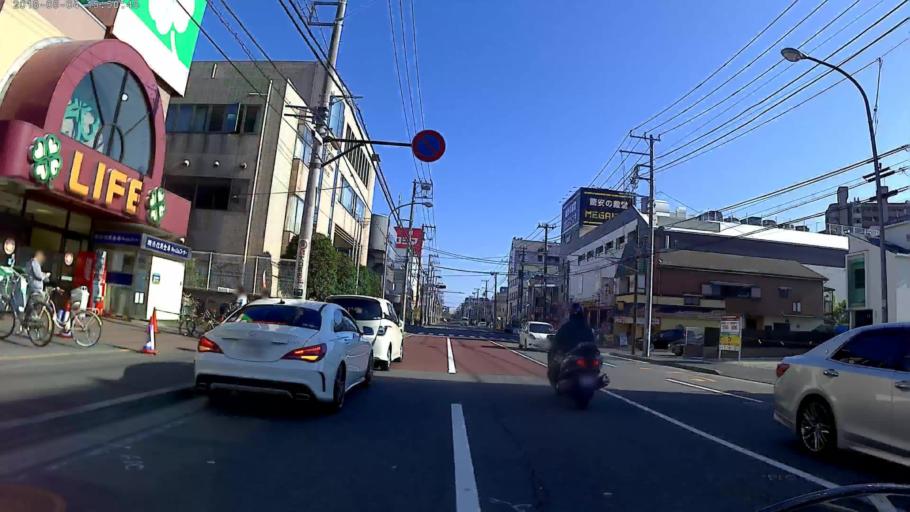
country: JP
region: Kanagawa
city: Yokohama
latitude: 35.4942
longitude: 139.6479
